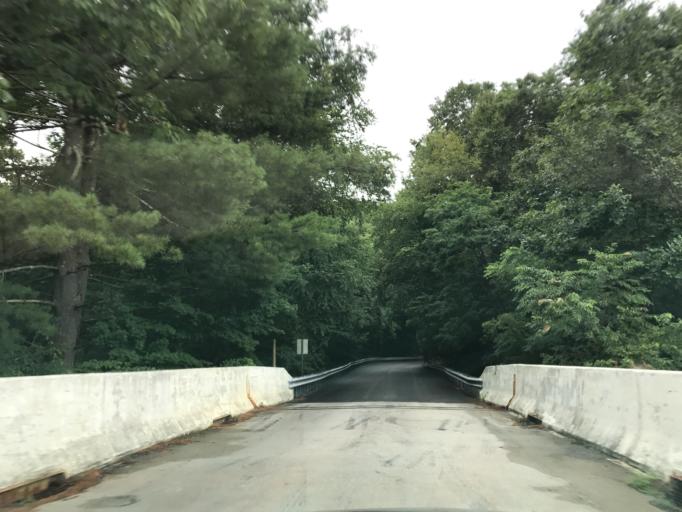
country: US
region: Pennsylvania
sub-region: York County
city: New Freedom
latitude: 39.6804
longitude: -76.7705
